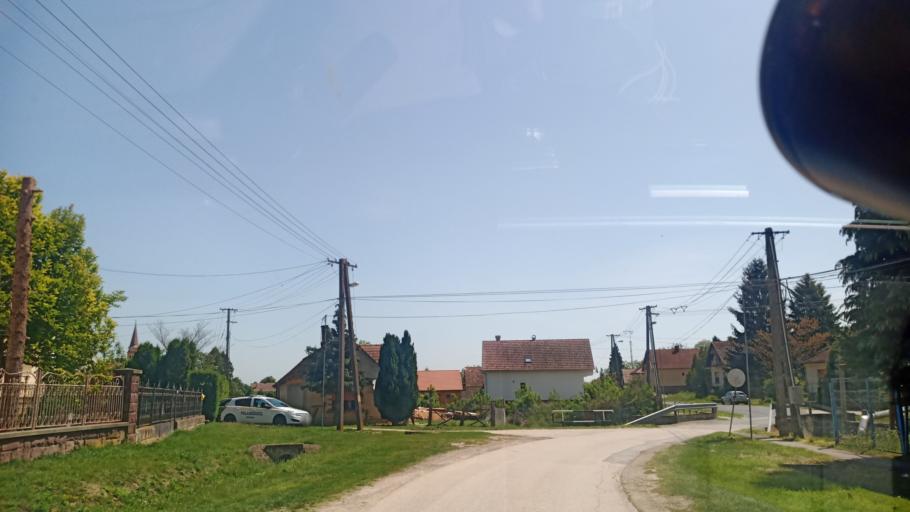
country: HU
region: Zala
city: Zalakomar
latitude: 46.6189
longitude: 17.1126
